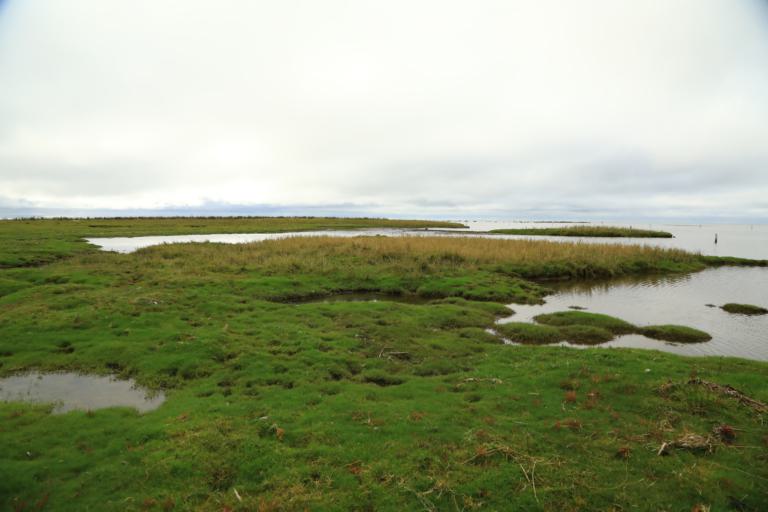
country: SE
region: Halland
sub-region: Varbergs Kommun
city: Traslovslage
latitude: 57.0190
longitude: 12.3356
